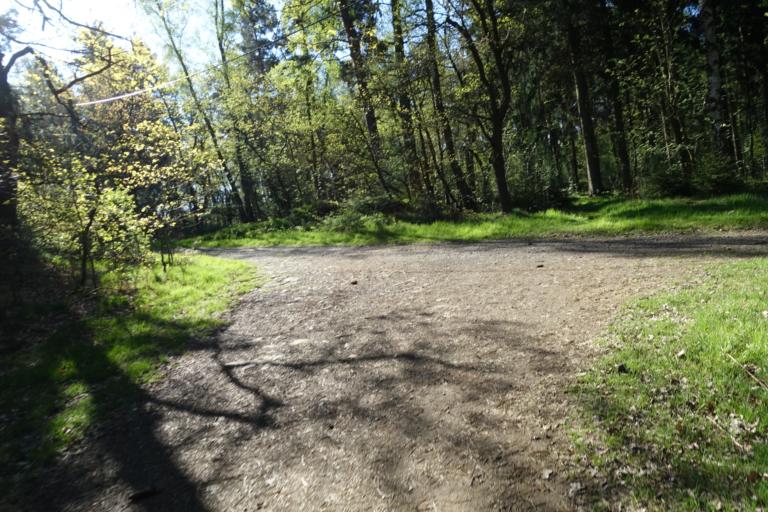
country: DE
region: Saxony
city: Freiberg
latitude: 50.8992
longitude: 13.3981
